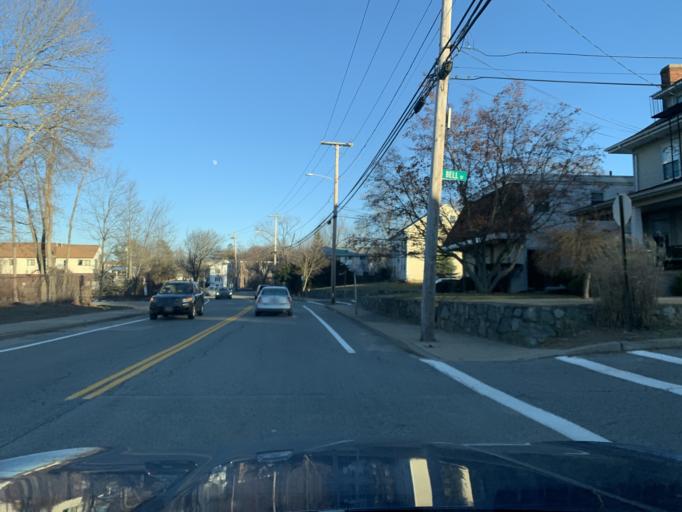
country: US
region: Rhode Island
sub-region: Kent County
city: West Warwick
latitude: 41.6958
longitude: -71.5255
